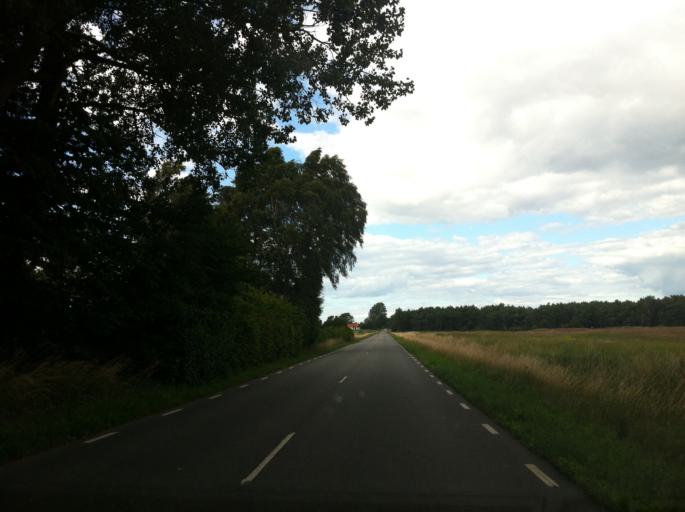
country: SE
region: Skane
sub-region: Simrishamns Kommun
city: Simrishamn
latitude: 55.4145
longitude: 14.2047
